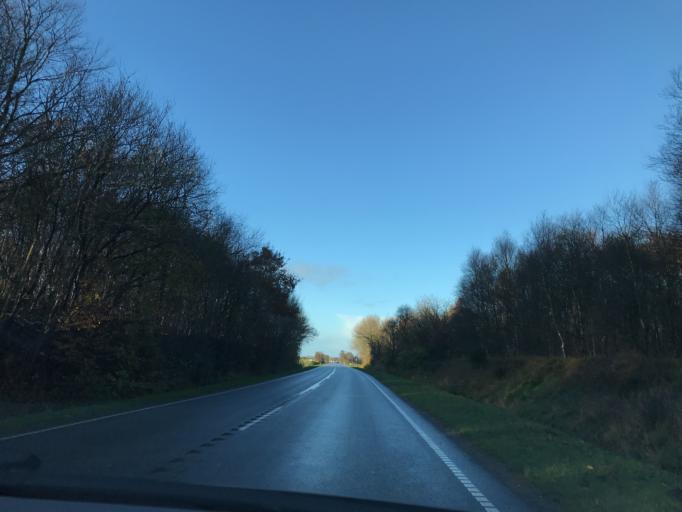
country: DK
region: South Denmark
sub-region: Haderslev Kommune
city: Vojens
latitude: 55.1726
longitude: 9.3440
